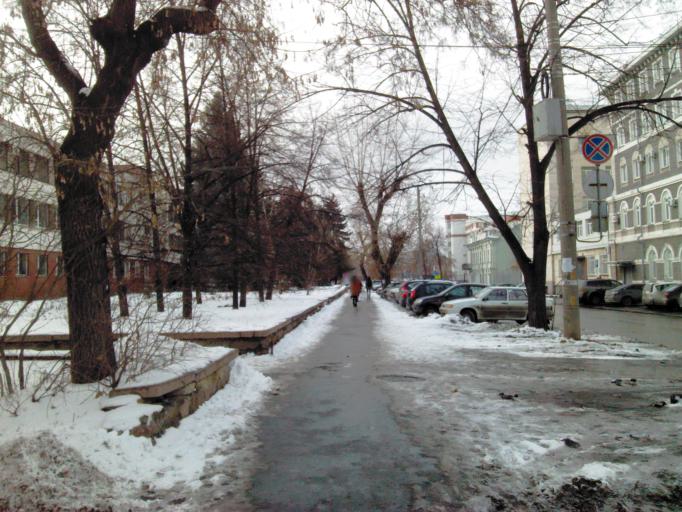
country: RU
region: Chelyabinsk
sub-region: Gorod Chelyabinsk
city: Chelyabinsk
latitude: 55.1626
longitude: 61.3983
